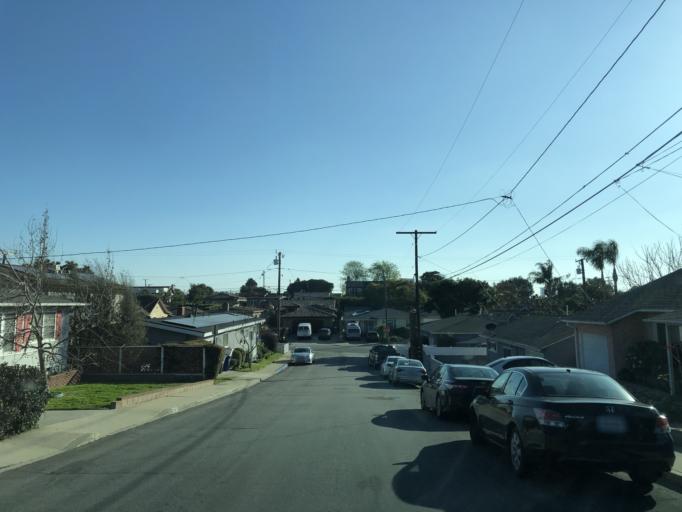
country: US
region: California
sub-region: Los Angeles County
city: El Segundo
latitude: 33.9296
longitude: -118.4121
